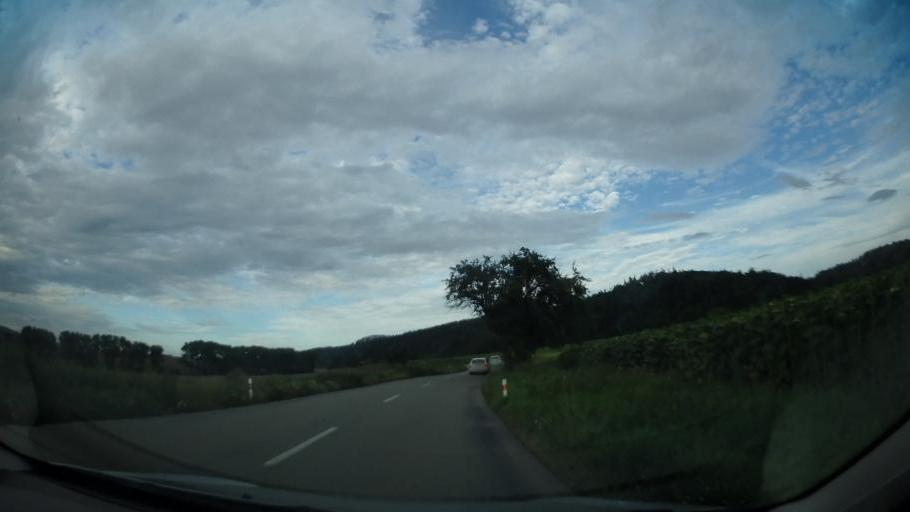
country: CZ
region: South Moravian
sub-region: Okres Blansko
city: Boskovice
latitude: 49.5107
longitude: 16.6730
